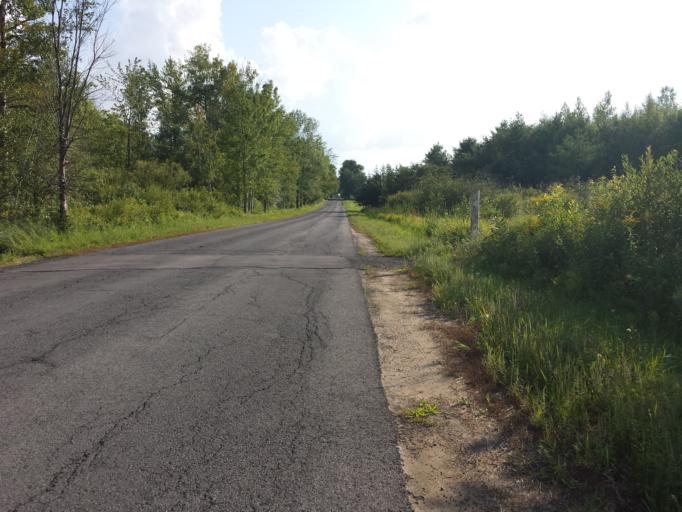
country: US
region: New York
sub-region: St. Lawrence County
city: Potsdam
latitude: 44.6906
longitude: -74.9304
